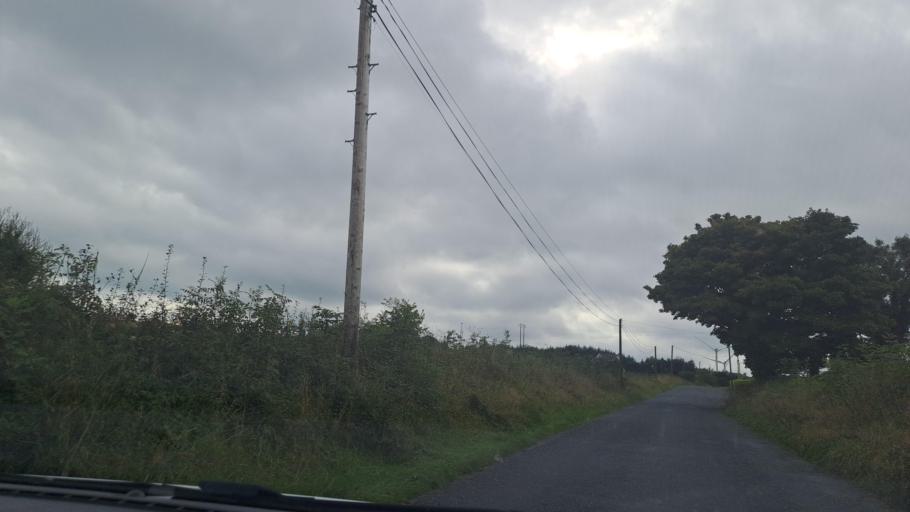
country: IE
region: Ulster
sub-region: An Cabhan
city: Kingscourt
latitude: 53.9651
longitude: -6.8707
